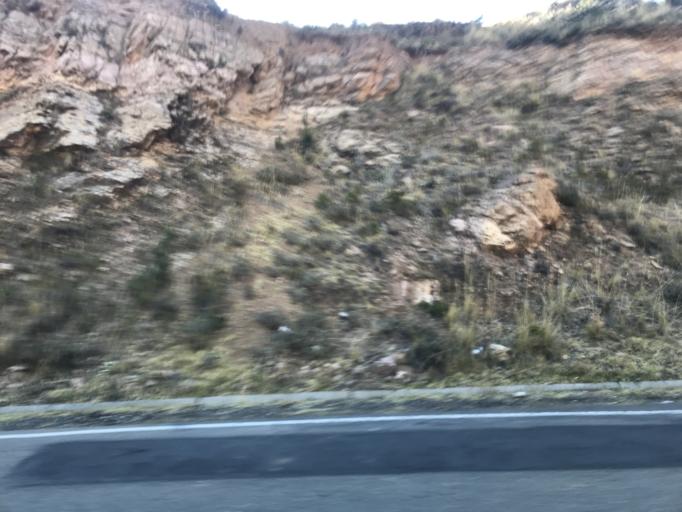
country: BO
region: La Paz
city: San Pedro
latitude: -16.2270
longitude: -68.8513
